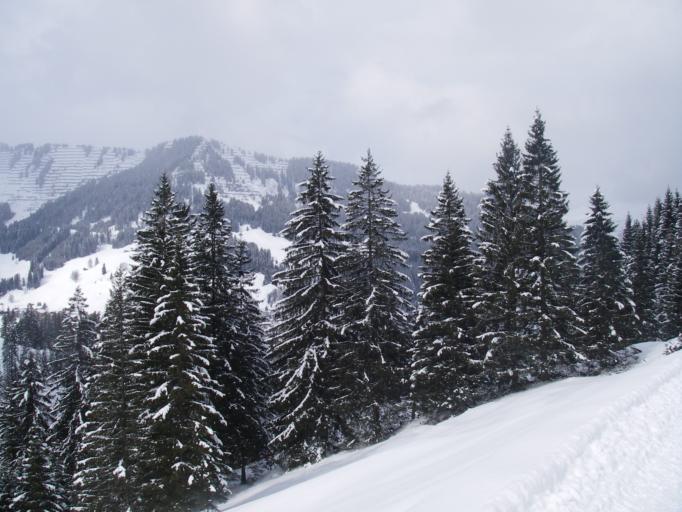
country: AT
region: Vorarlberg
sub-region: Politischer Bezirk Bregenz
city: Mittelberg
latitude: 47.3214
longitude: 10.1758
